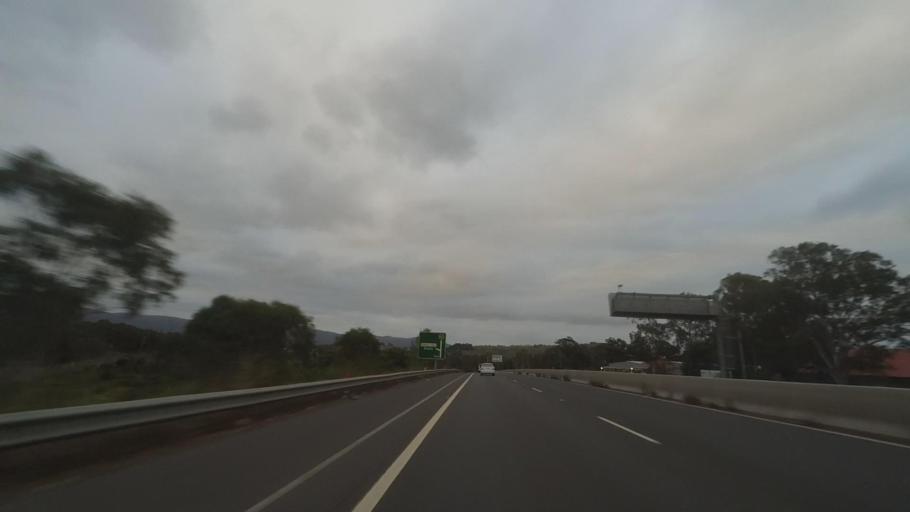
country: AU
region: New South Wales
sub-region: Shellharbour
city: Albion Park Rail
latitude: -34.5368
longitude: 150.7855
